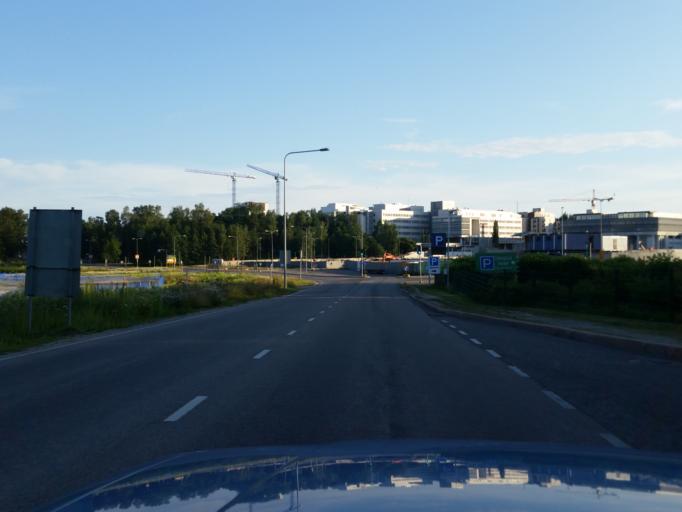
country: FI
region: Uusimaa
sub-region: Helsinki
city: Otaniemi
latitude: 60.1772
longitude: 24.8109
